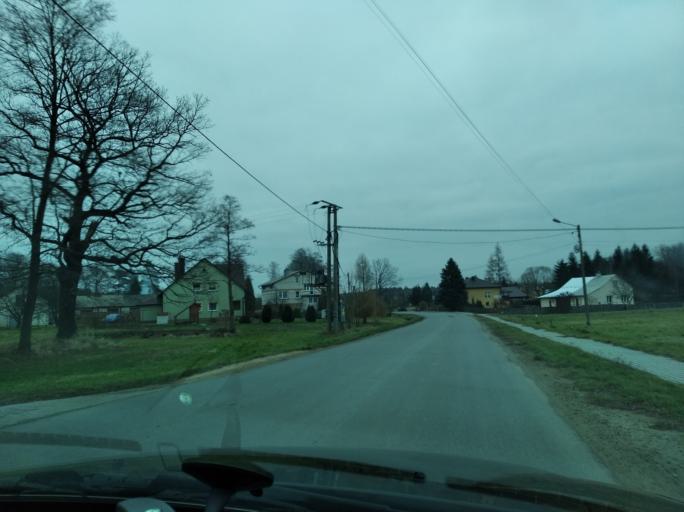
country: PL
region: Subcarpathian Voivodeship
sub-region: Powiat lancucki
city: Rakszawa
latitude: 50.1647
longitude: 22.2027
